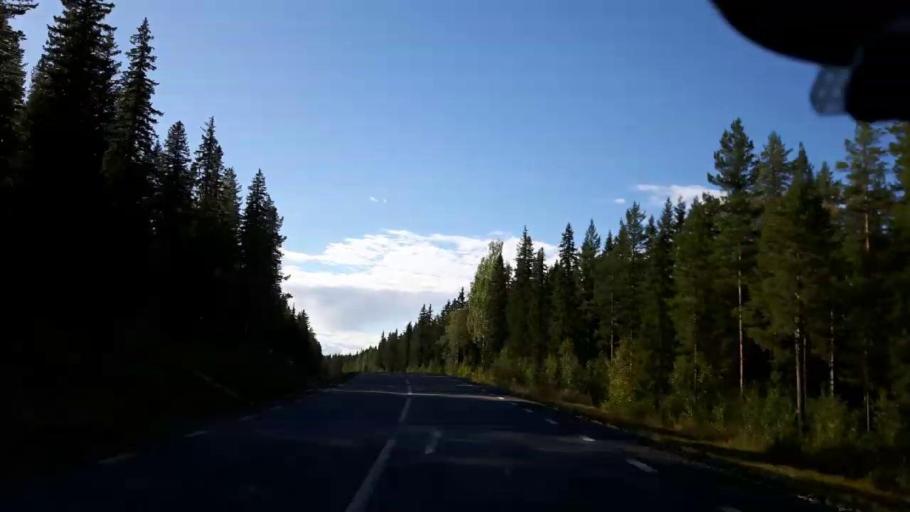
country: SE
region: Jaemtland
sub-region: Ragunda Kommun
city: Hammarstrand
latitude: 63.5362
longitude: 16.0358
